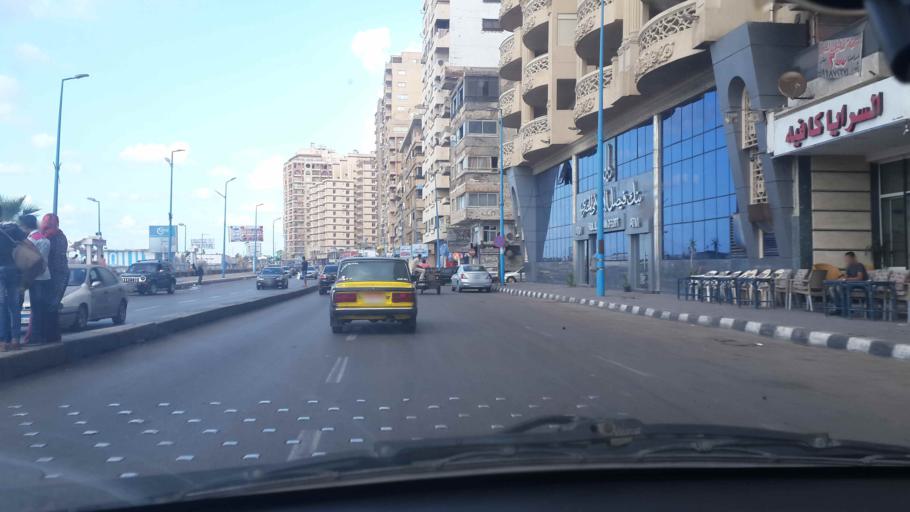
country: EG
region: Alexandria
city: Alexandria
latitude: 31.2731
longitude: 30.0005
